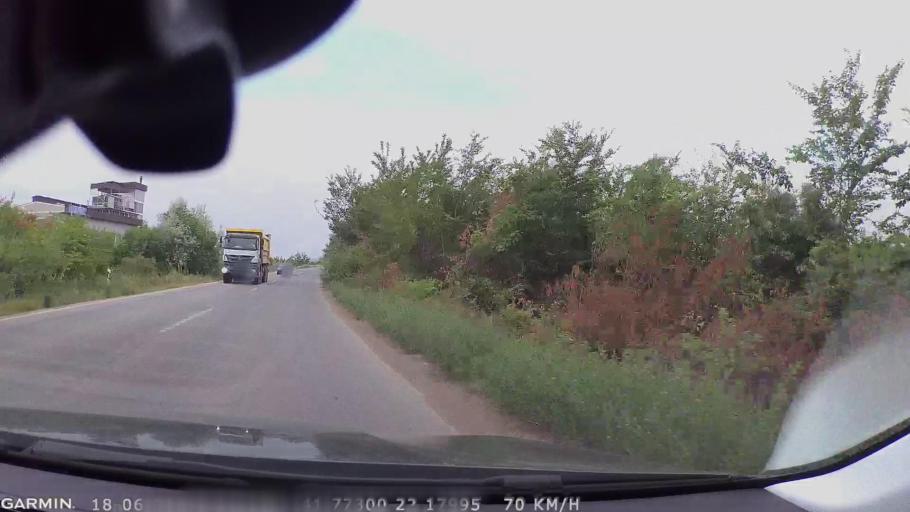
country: MK
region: Stip
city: Shtip
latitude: 41.7729
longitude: 22.1798
